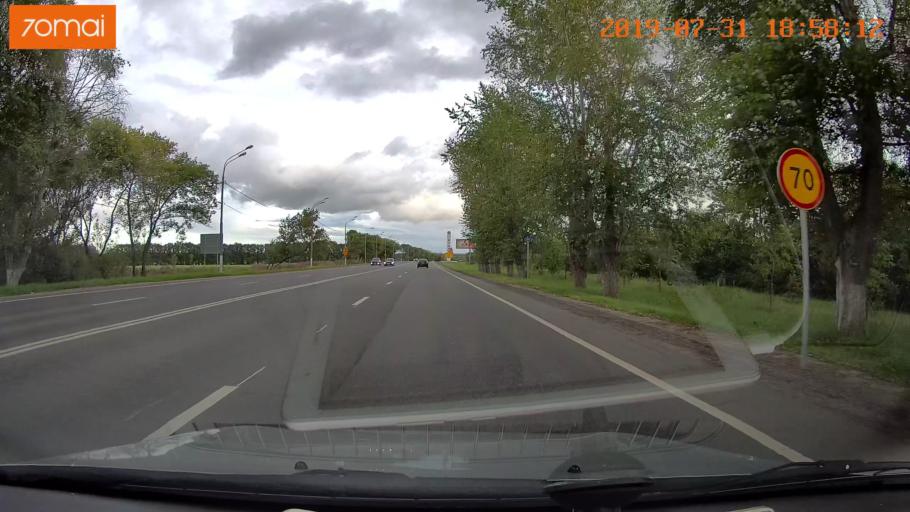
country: RU
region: Moskovskaya
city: Raduzhnyy
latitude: 55.1486
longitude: 38.7015
